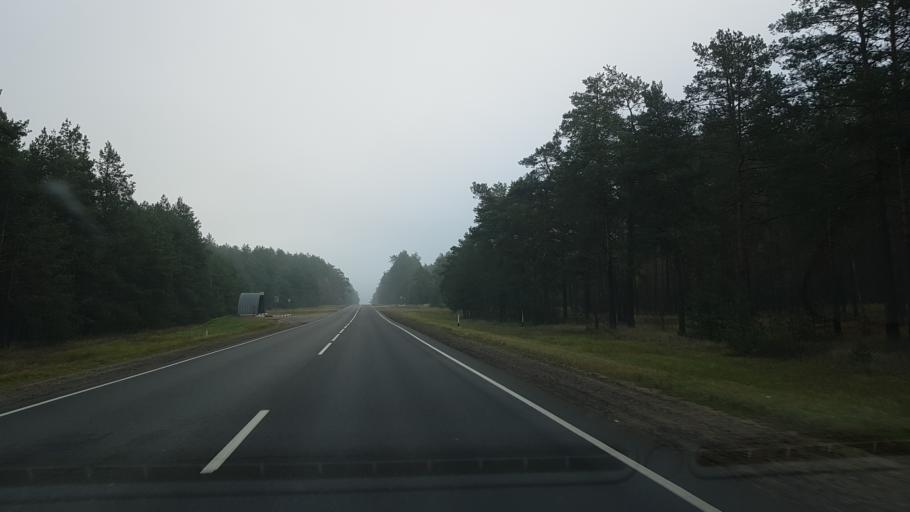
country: BY
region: Mogilev
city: Babruysk
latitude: 53.1604
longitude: 29.3221
